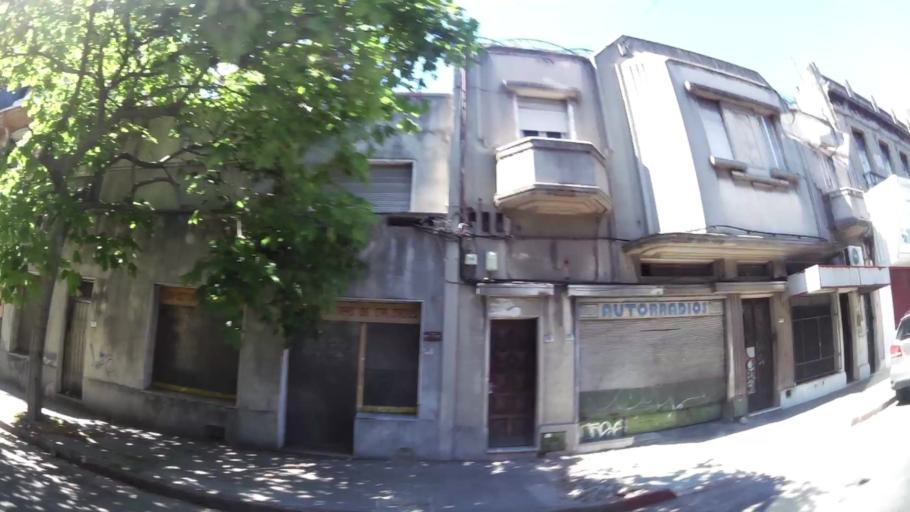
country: UY
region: Montevideo
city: Montevideo
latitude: -34.9018
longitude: -56.1990
